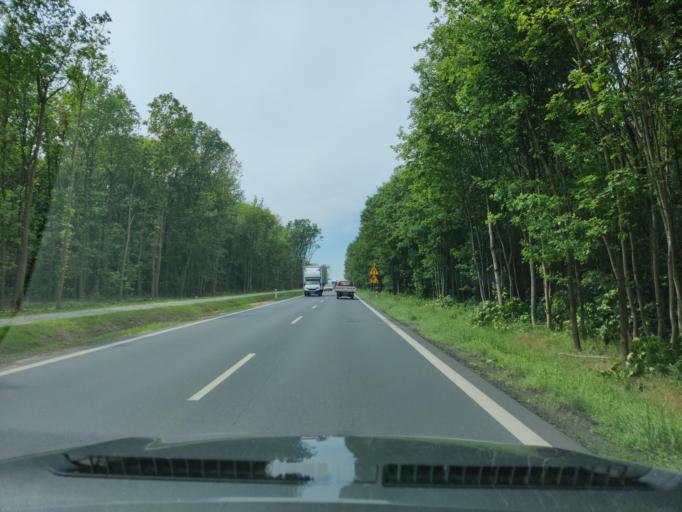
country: PL
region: Greater Poland Voivodeship
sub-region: Powiat grodziski
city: Granowo
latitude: 52.2304
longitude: 16.5942
